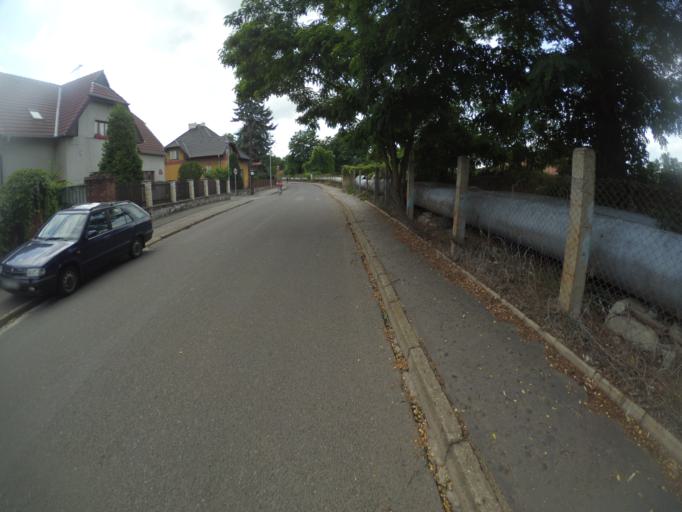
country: CZ
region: Central Bohemia
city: Neratovice
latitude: 50.2619
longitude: 14.5201
